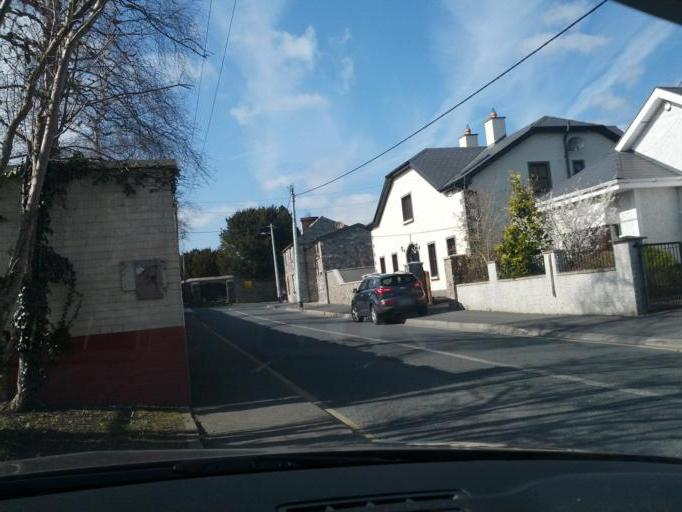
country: IE
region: Leinster
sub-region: Kildare
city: Celbridge
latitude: 53.3384
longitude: -6.5452
